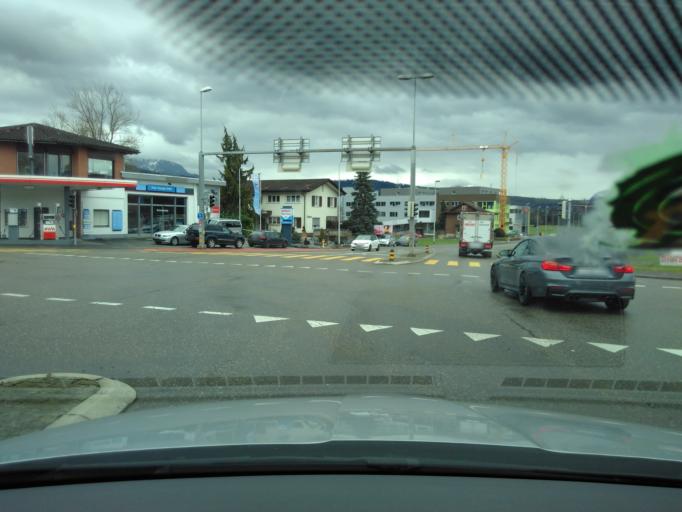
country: CH
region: Lucerne
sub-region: Hochdorf District
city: Inwil
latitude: 47.1218
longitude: 8.3412
